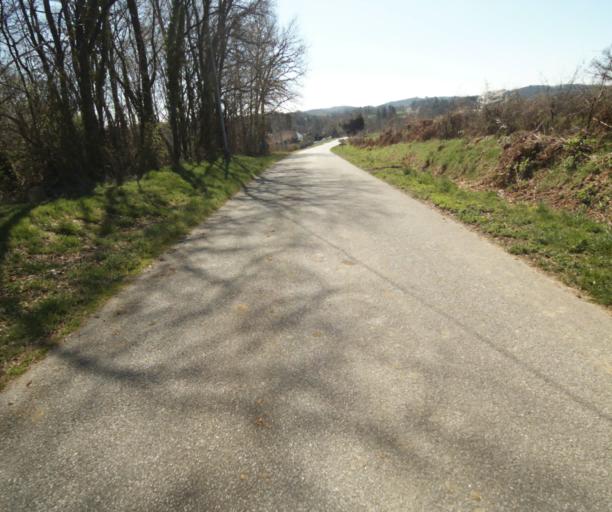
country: FR
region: Limousin
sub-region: Departement de la Correze
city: Saint-Mexant
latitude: 45.3132
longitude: 1.6468
